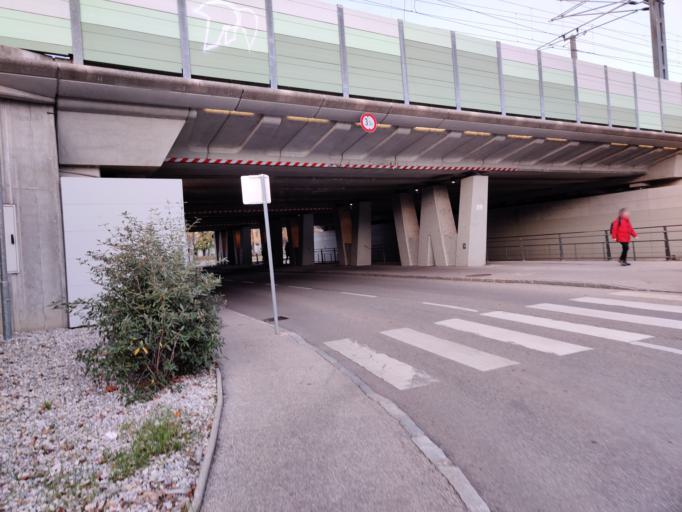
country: AT
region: Lower Austria
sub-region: Sankt Polten Stadt
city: Sankt Poelten
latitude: 48.2078
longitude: 15.6293
